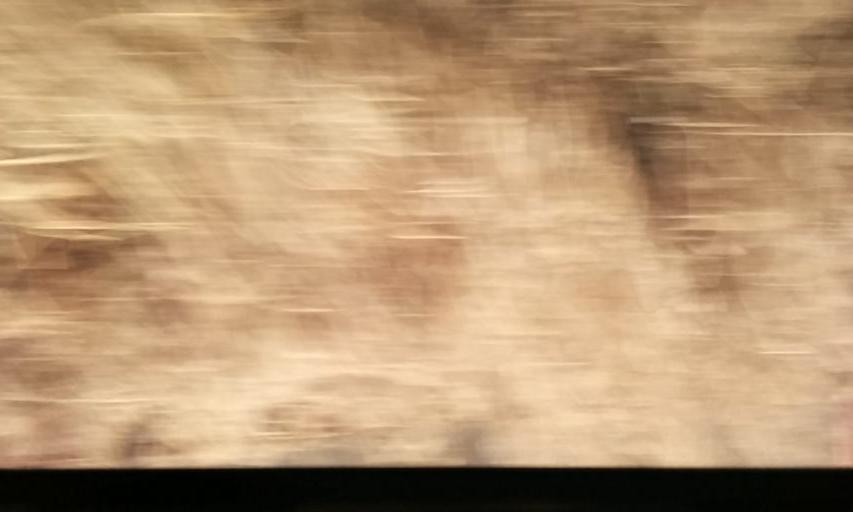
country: JP
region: Nagano
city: Tatsuno
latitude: 36.0068
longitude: 137.8558
